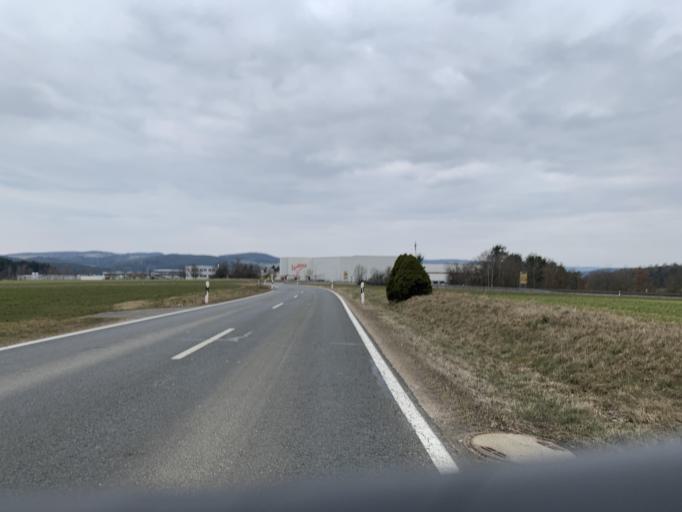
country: DE
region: Bavaria
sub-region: Upper Palatinate
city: Neunburg vorm Wald
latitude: 49.3369
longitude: 12.4099
